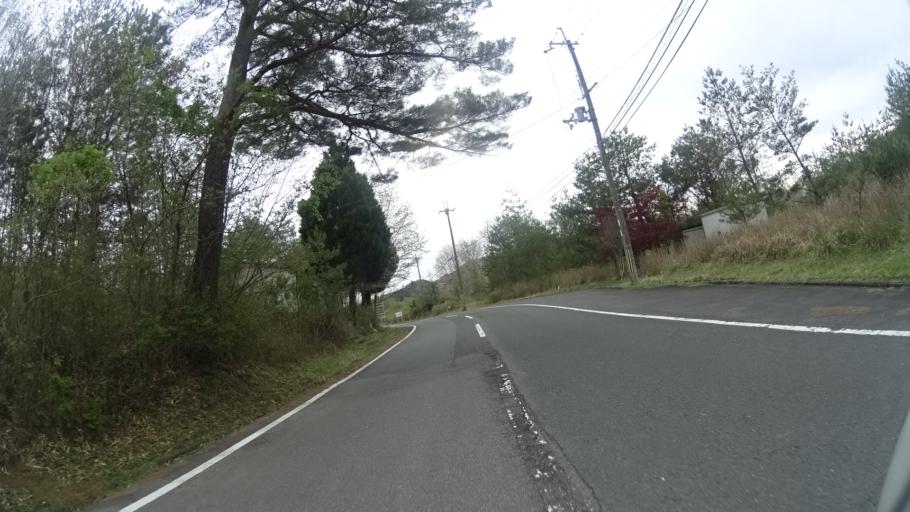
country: JP
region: Kyoto
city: Ayabe
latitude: 35.2089
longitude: 135.4595
